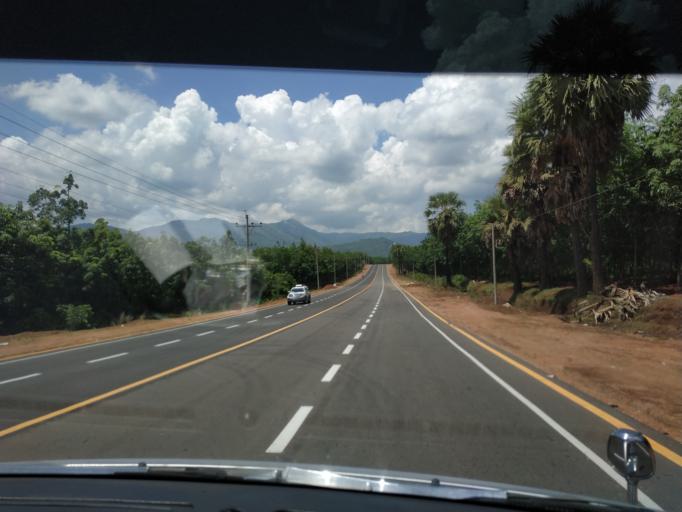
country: MM
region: Mon
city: Kyaikto
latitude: 17.3838
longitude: 97.0561
